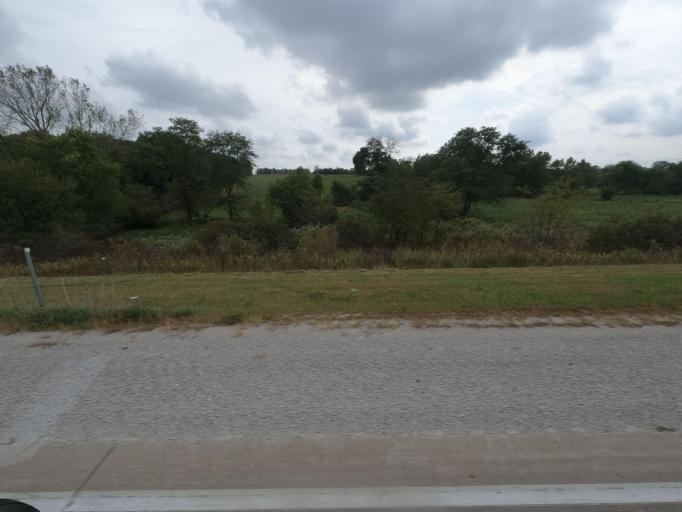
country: US
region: Iowa
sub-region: Wapello County
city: Ottumwa
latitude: 41.0032
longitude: -92.2802
